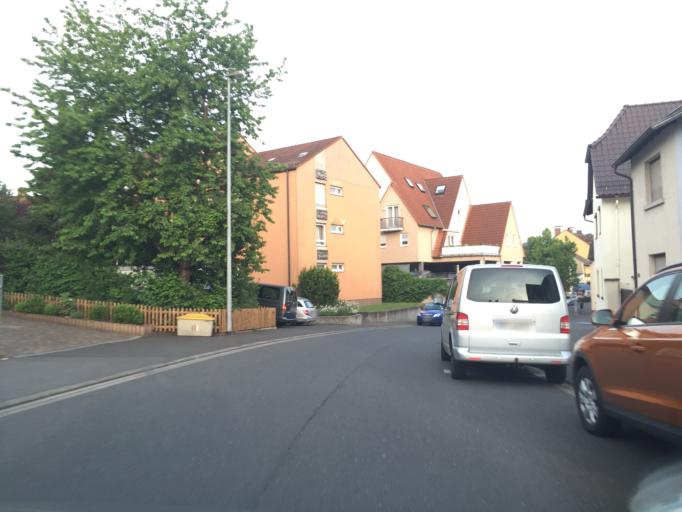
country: DE
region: Bavaria
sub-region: Regierungsbezirk Unterfranken
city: Aschaffenburg
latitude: 49.9595
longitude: 9.1646
